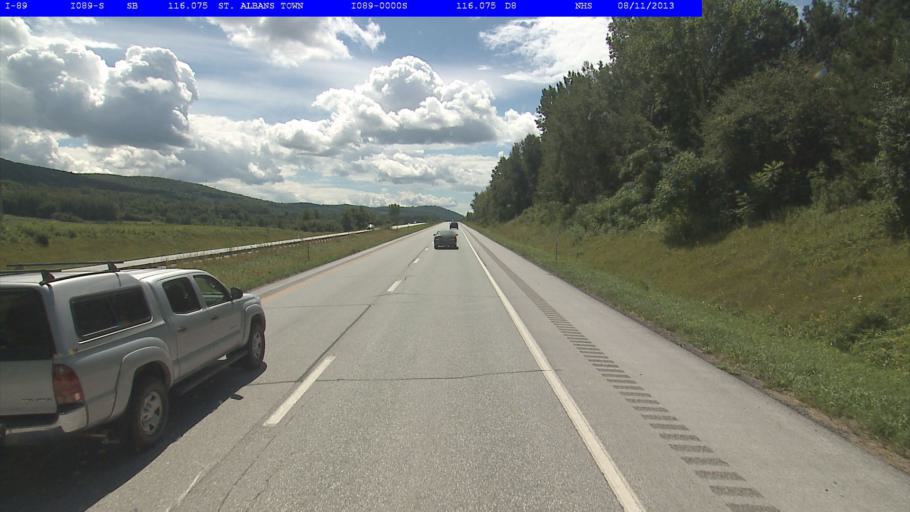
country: US
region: Vermont
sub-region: Franklin County
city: Saint Albans
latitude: 44.8278
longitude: -73.0622
